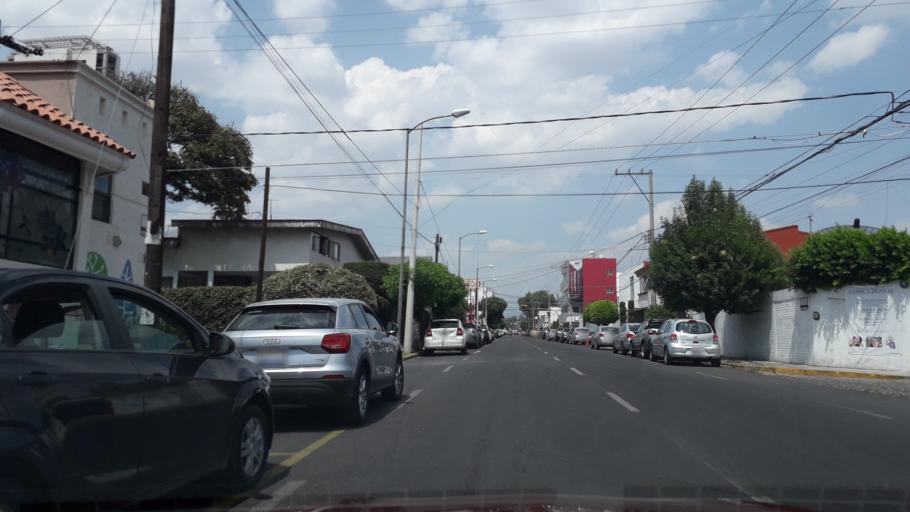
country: MX
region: Puebla
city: Puebla
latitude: 19.0313
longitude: -98.2222
